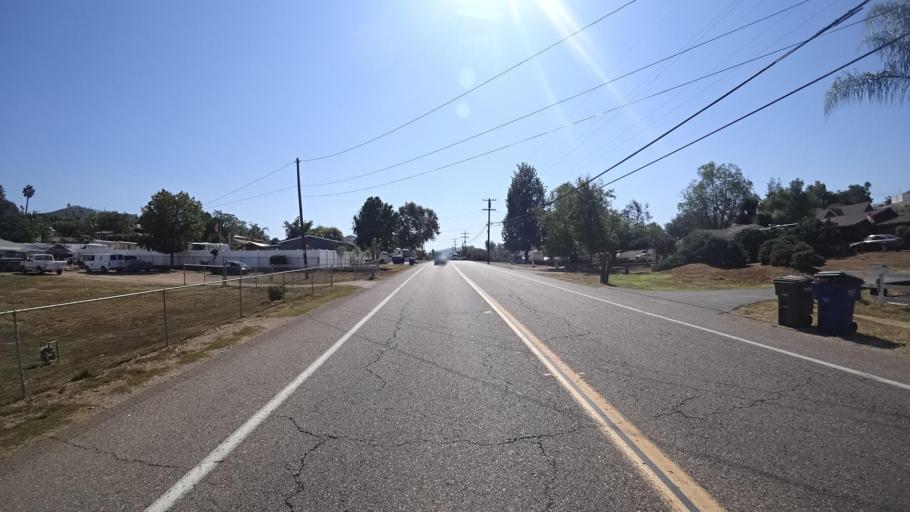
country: US
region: California
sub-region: San Diego County
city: Granite Hills
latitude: 32.8055
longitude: -116.9088
